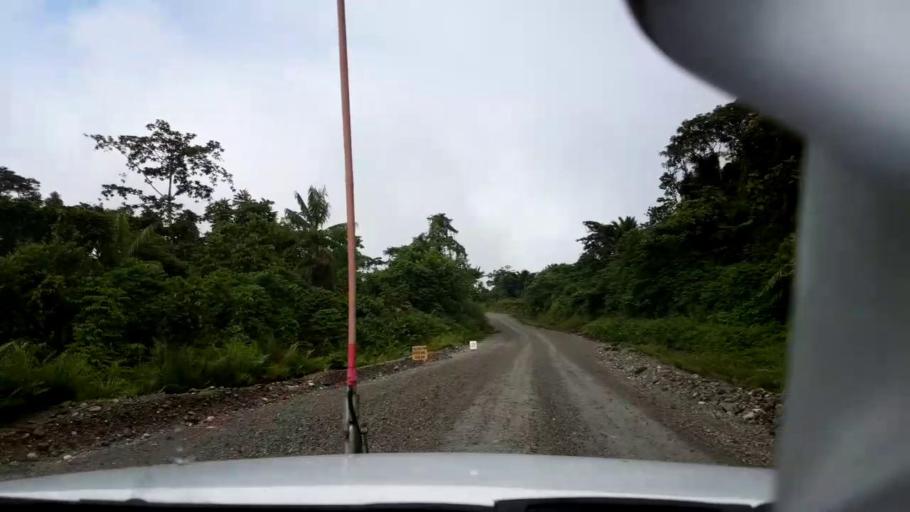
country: PG
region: Western Province
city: Kiunga
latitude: -5.5233
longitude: 141.2794
